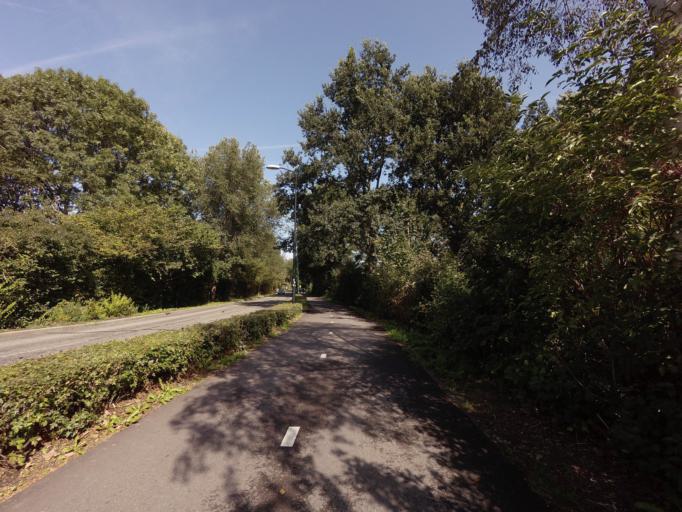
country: NL
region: Utrecht
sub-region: Gemeente De Ronde Venen
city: Mijdrecht
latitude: 52.2102
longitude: 4.8614
